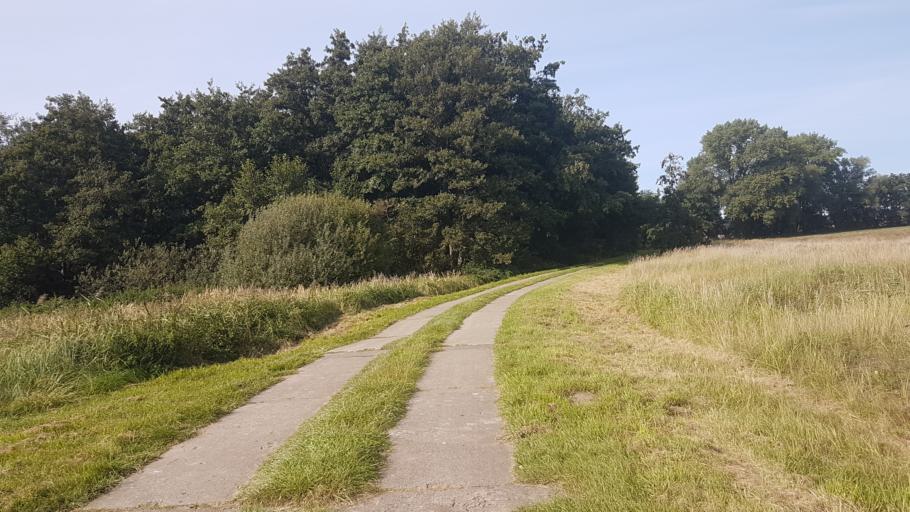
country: DE
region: Mecklenburg-Vorpommern
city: Gingst
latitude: 54.4338
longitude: 13.2048
